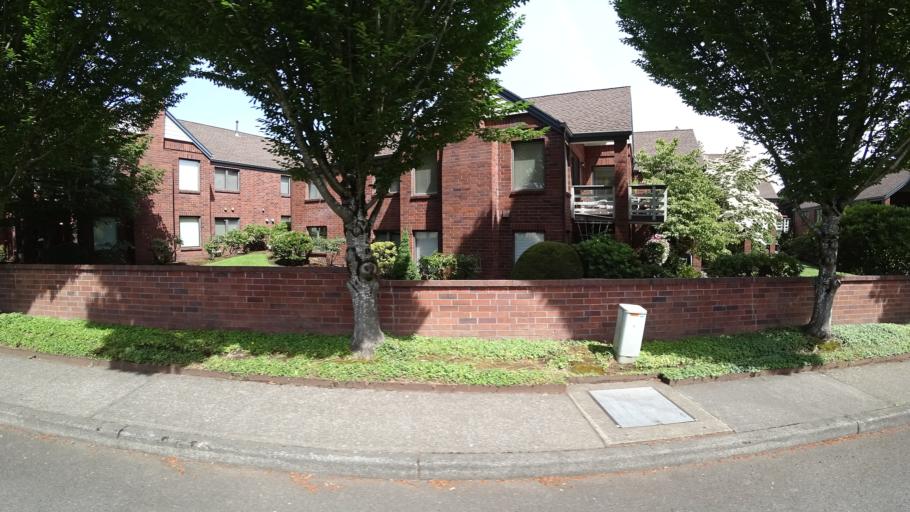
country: US
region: Oregon
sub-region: Multnomah County
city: Fairview
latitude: 45.5416
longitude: -122.5067
